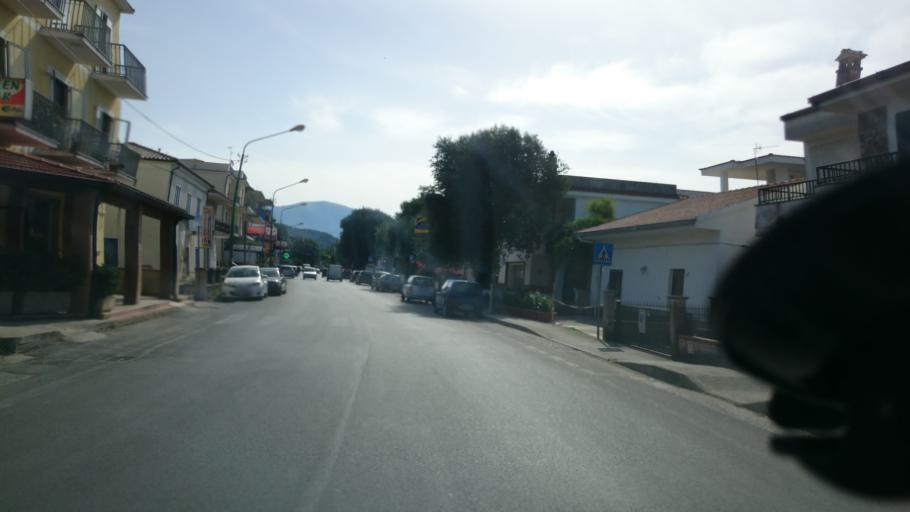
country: IT
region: Campania
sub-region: Provincia di Salerno
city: Policastro Bussentino
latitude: 40.0736
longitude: 15.5158
